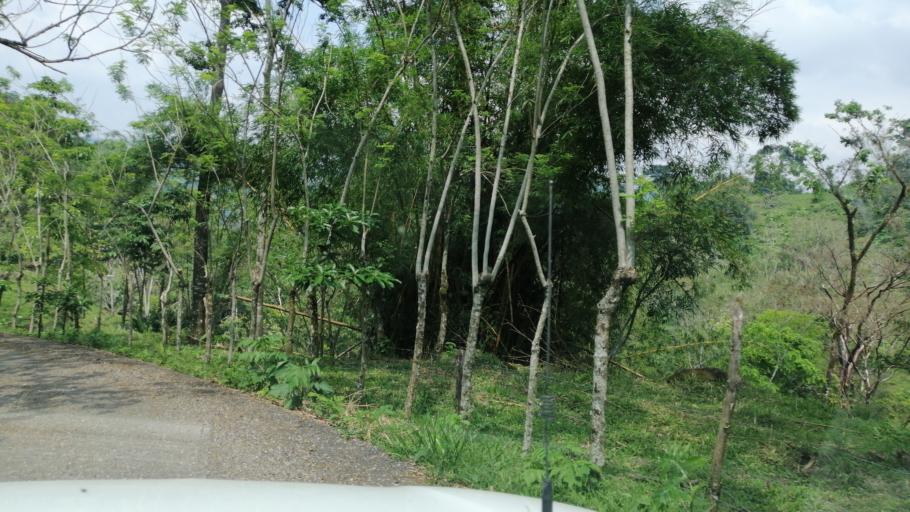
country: MX
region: Chiapas
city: Ostuacan
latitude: 17.3882
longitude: -93.3298
